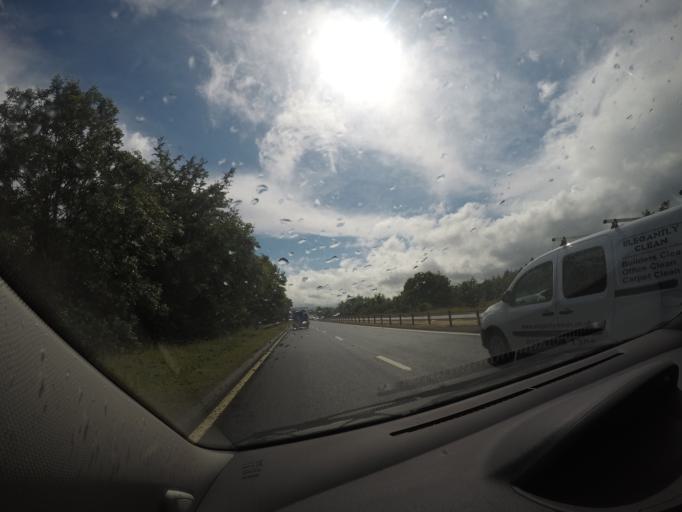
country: GB
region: Scotland
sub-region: Perth and Kinross
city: Auchterarder
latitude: 56.3116
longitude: -3.6607
